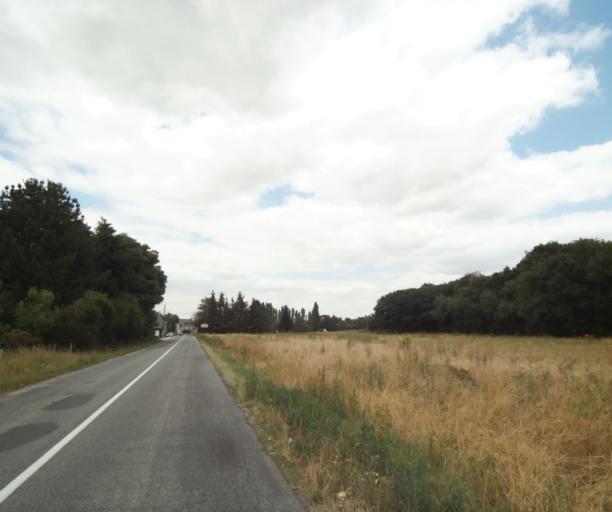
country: FR
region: Centre
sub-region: Departement du Loiret
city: Vennecy
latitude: 47.9312
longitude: 2.0445
